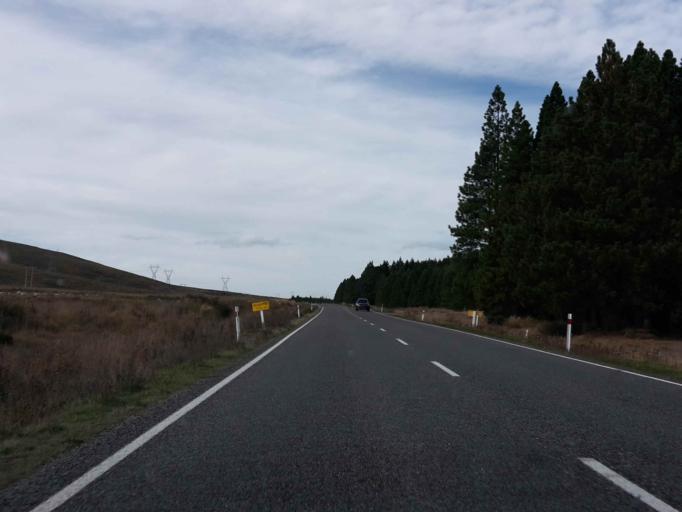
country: NZ
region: Canterbury
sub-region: Timaru District
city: Pleasant Point
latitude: -44.0910
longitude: 170.5862
